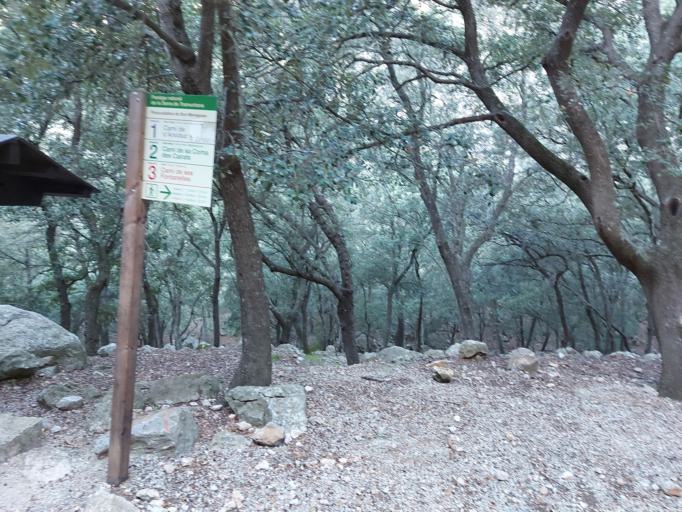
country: ES
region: Balearic Islands
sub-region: Illes Balears
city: Valldemossa
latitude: 39.7203
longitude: 2.6458
